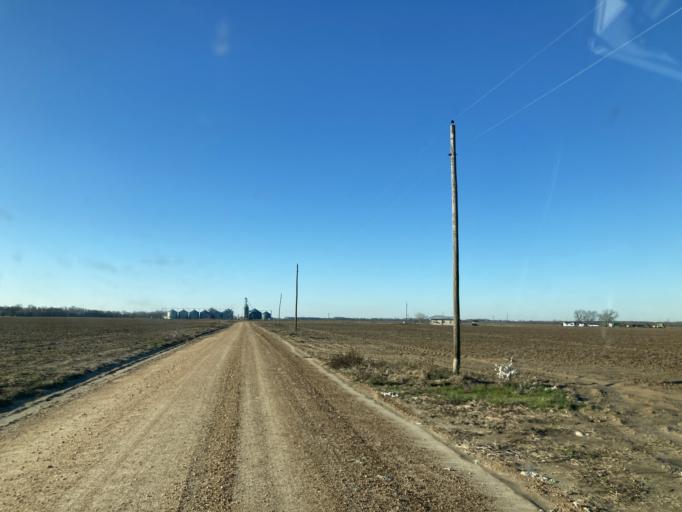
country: US
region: Mississippi
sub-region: Yazoo County
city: Yazoo City
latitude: 32.9247
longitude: -90.6139
